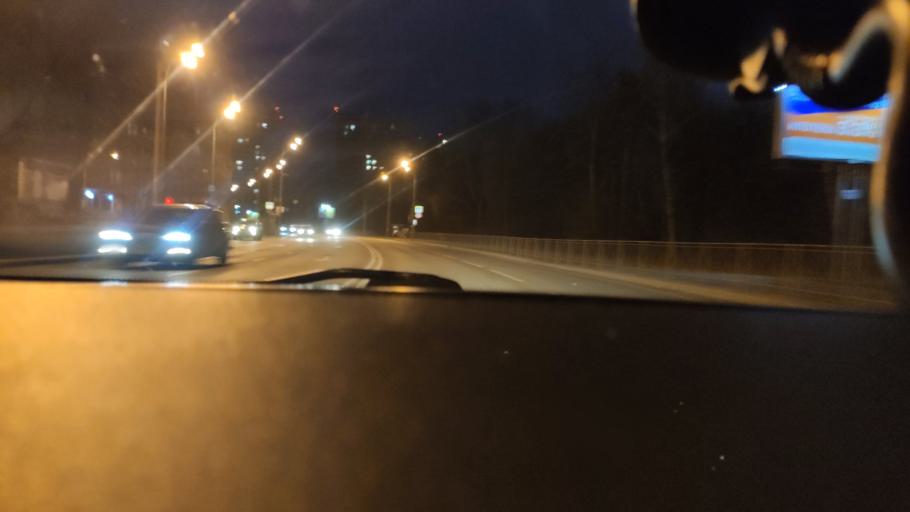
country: RU
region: Perm
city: Perm
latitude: 57.9951
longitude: 56.1924
